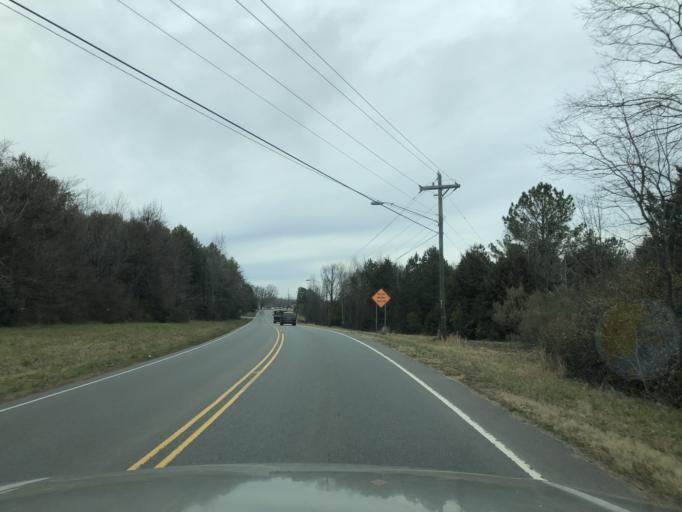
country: US
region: North Carolina
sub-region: Cleveland County
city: Shelby
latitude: 35.3035
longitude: -81.4864
